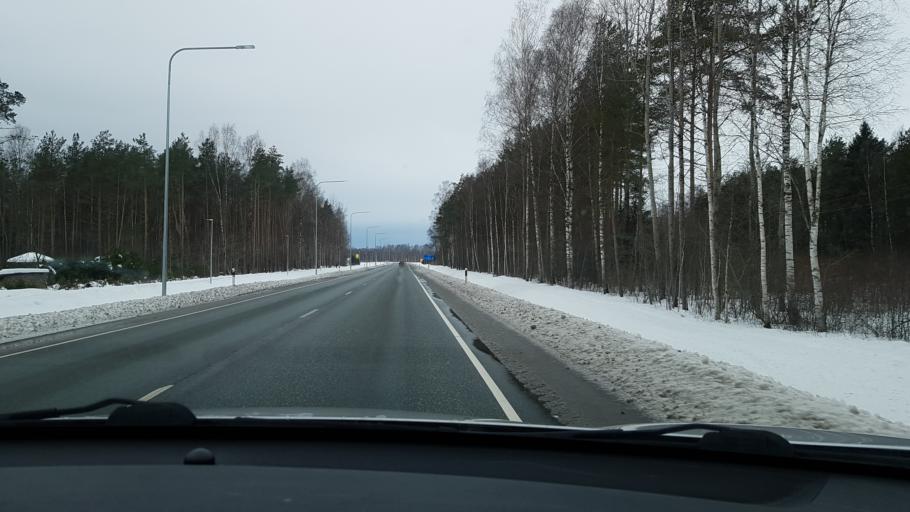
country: EE
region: Jaervamaa
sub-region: Paide linn
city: Paide
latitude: 58.8906
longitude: 25.5507
